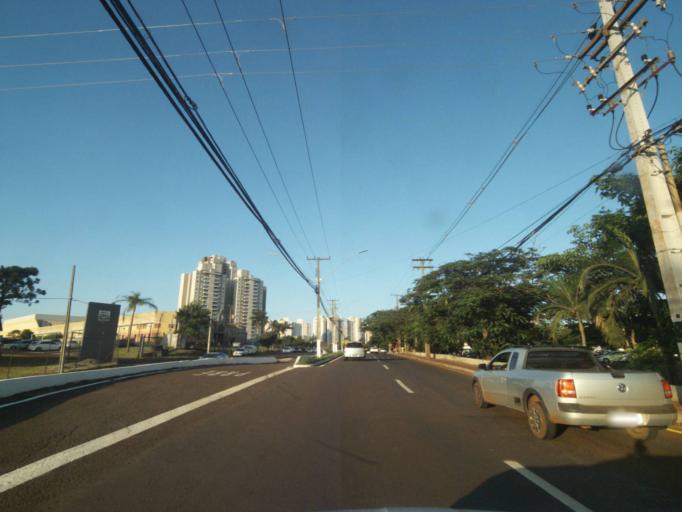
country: BR
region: Parana
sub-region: Londrina
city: Londrina
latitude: -23.3404
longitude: -51.1876
